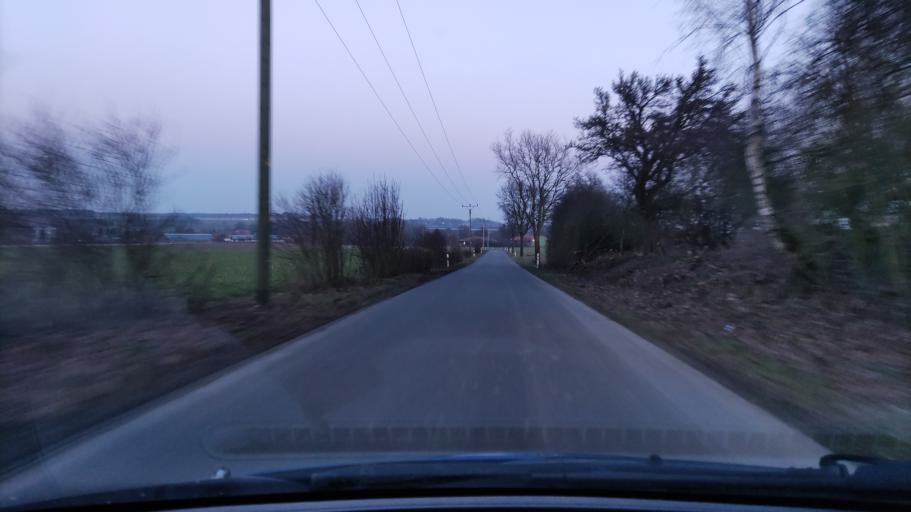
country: DE
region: Lower Saxony
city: Barum
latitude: 53.0533
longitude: 10.5024
